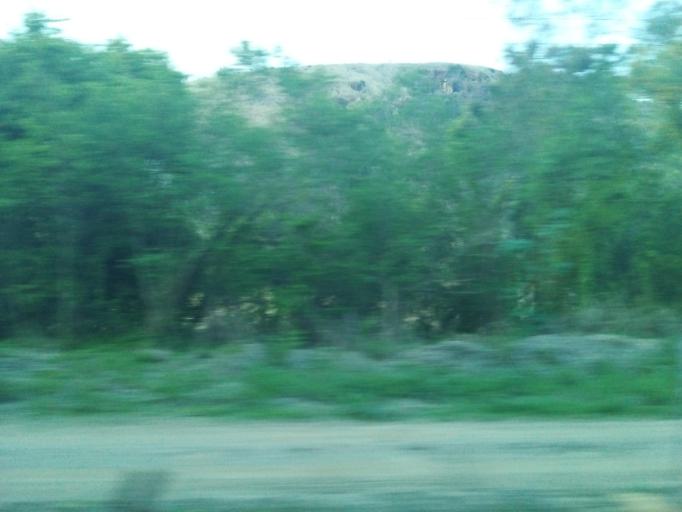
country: BR
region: Espirito Santo
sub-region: Baixo Guandu
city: Baixo Guandu
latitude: -19.5221
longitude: -40.8358
